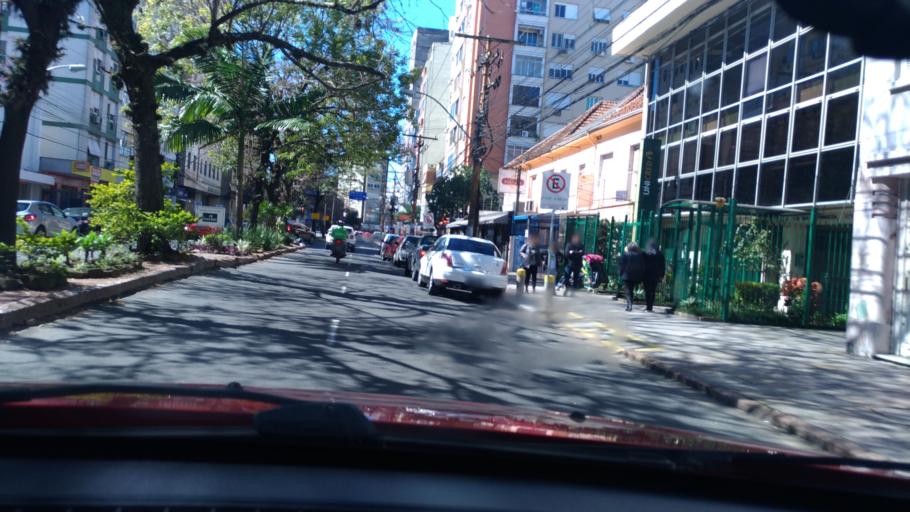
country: BR
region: Rio Grande do Sul
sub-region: Porto Alegre
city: Porto Alegre
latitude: -30.0378
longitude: -51.2106
